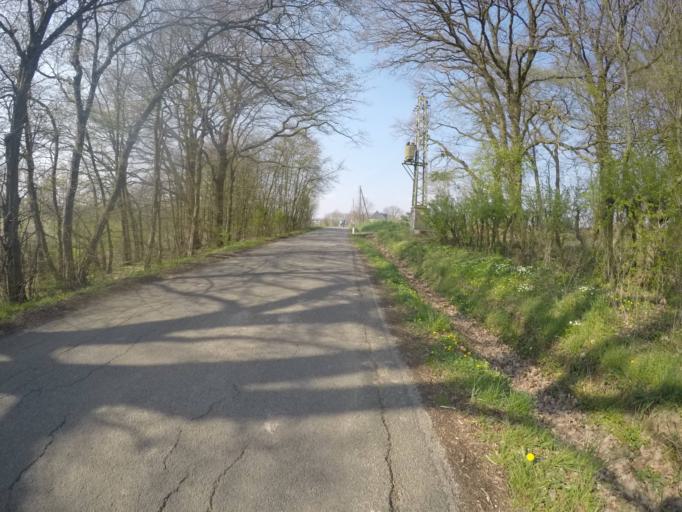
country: DE
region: North Rhine-Westphalia
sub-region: Regierungsbezirk Detmold
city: Bielefeld
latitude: 52.0473
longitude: 8.6129
